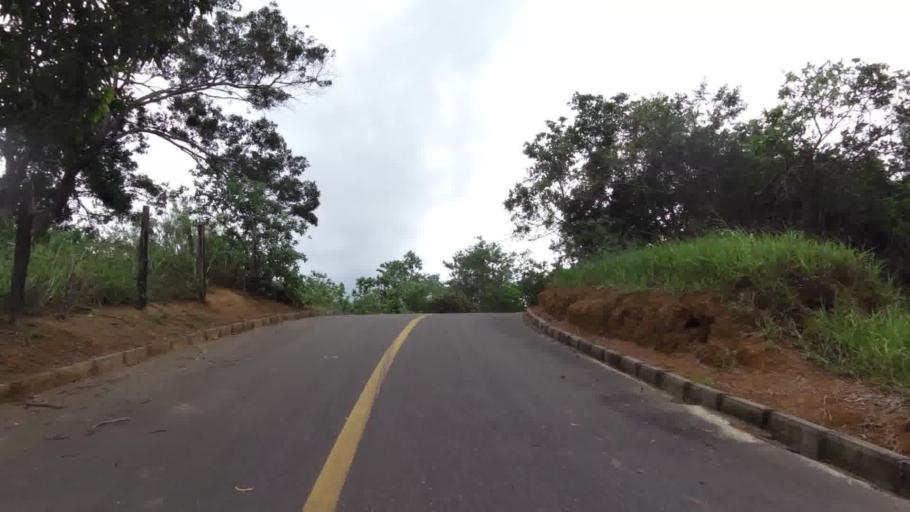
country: BR
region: Espirito Santo
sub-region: Piuma
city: Piuma
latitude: -20.8018
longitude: -40.6464
